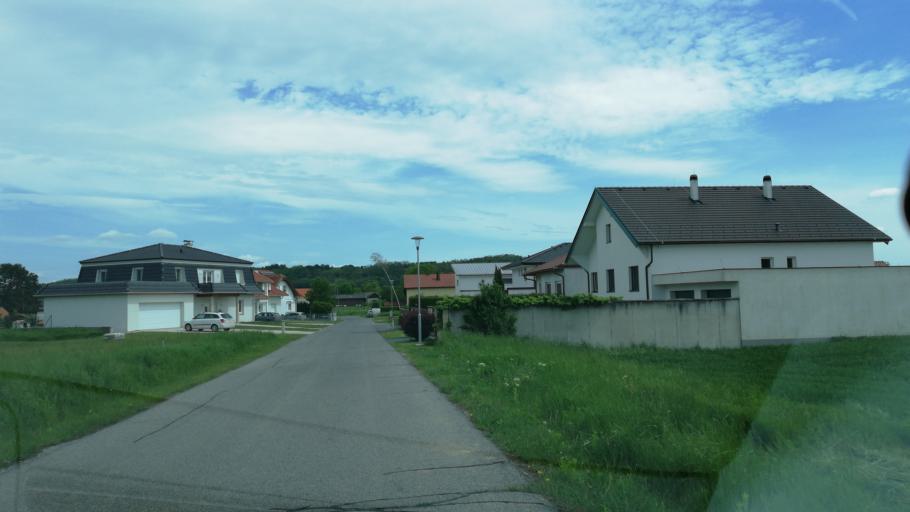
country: AT
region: Burgenland
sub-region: Politischer Bezirk Oberpullendorf
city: Lutzmannsburg
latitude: 47.4548
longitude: 16.6076
